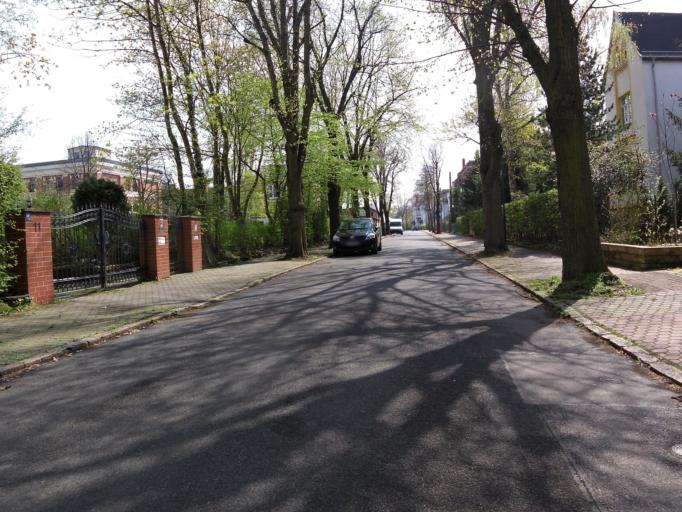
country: DE
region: Saxony
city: Markranstadt
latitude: 51.3262
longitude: 12.2522
